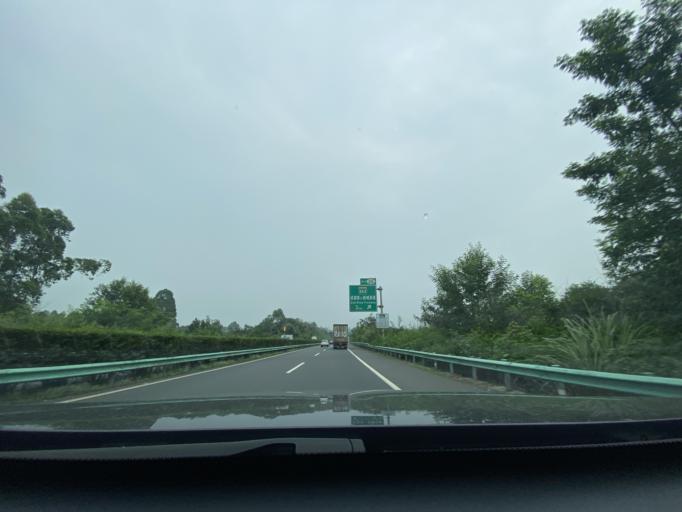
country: CN
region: Sichuan
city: Longquan
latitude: 30.3104
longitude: 104.1187
